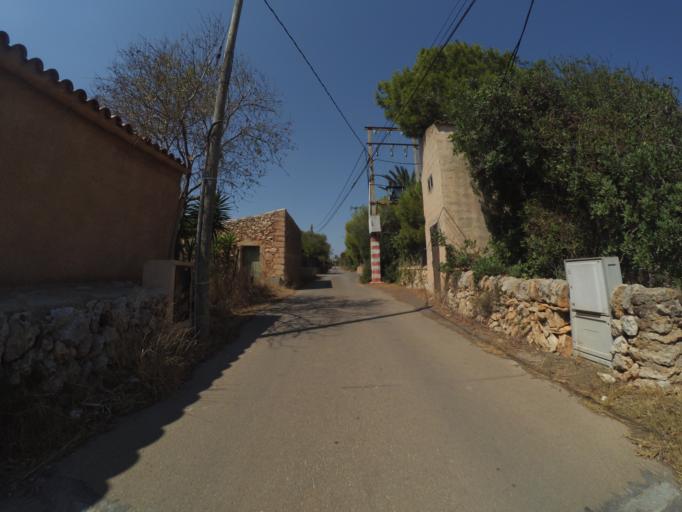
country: ES
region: Balearic Islands
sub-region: Illes Balears
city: Santanyi
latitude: 39.3903
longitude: 3.2387
